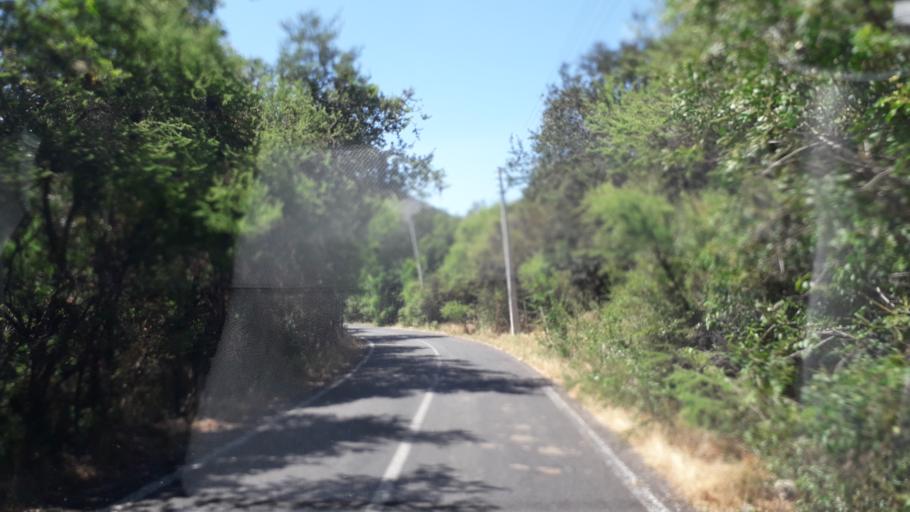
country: CL
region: Valparaiso
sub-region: Provincia de Marga Marga
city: Limache
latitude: -33.0704
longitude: -71.2191
